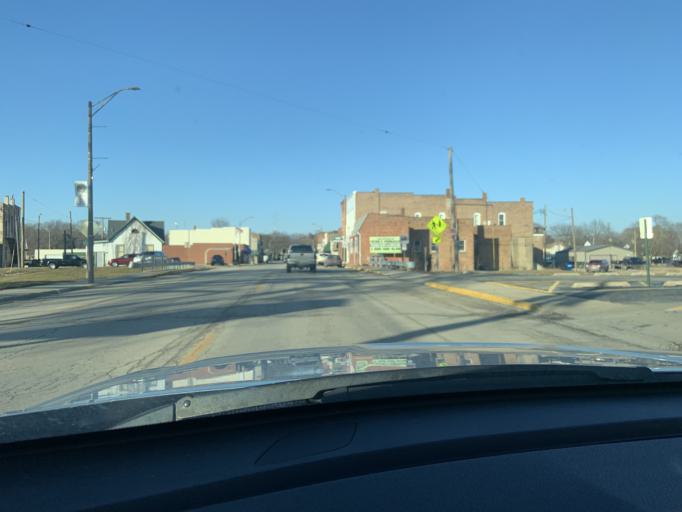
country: US
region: Illinois
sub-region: LaSalle County
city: Seneca
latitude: 41.3147
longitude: -88.6099
